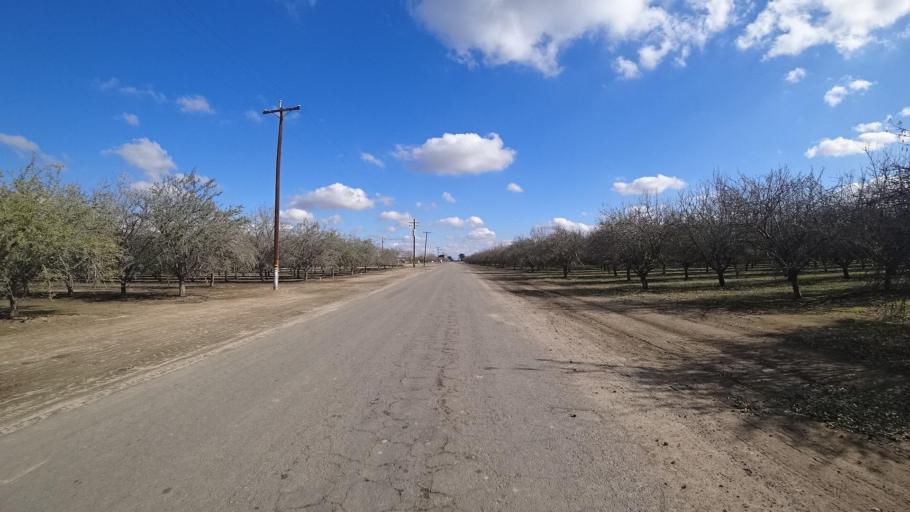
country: US
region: California
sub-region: Kern County
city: Delano
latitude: 35.7467
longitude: -119.3516
